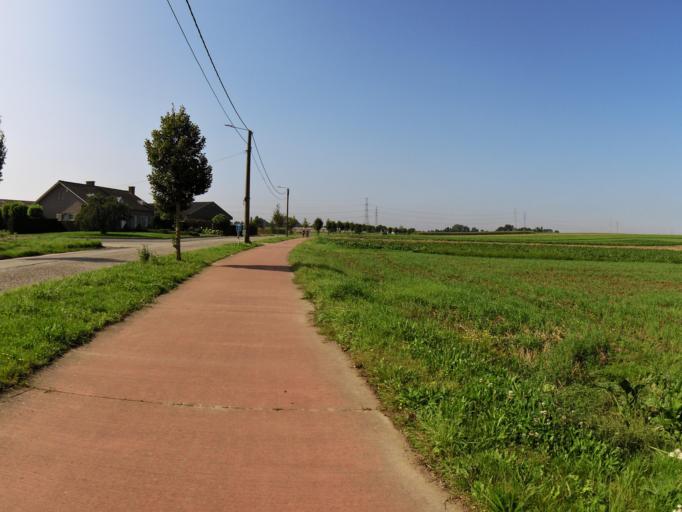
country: BE
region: Flanders
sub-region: Provincie Limburg
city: Riemst
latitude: 50.8021
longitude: 5.6025
